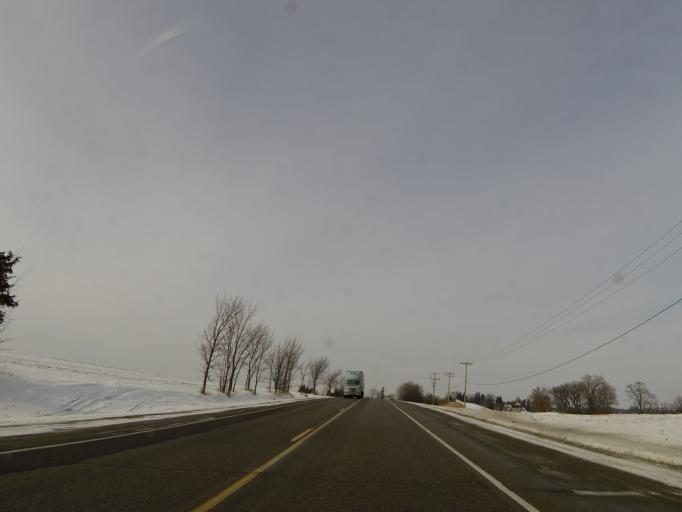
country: US
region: Minnesota
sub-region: Hennepin County
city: Saint Bonifacius
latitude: 44.8961
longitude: -93.7153
